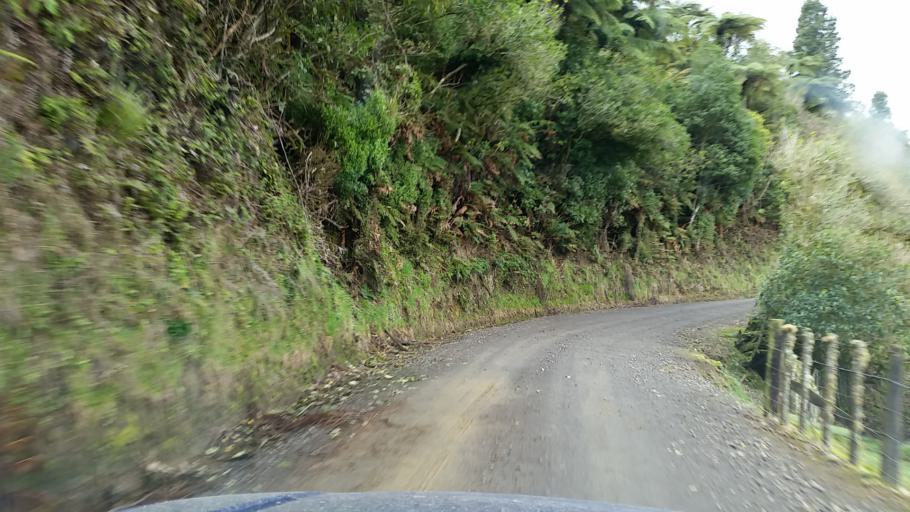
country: NZ
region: Taranaki
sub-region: South Taranaki District
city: Eltham
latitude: -39.1693
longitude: 174.6276
